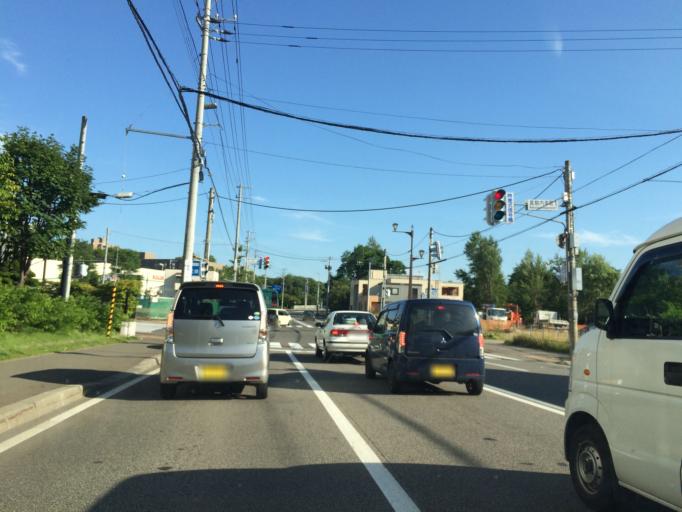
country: JP
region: Hokkaido
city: Sapporo
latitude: 42.9910
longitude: 141.3508
